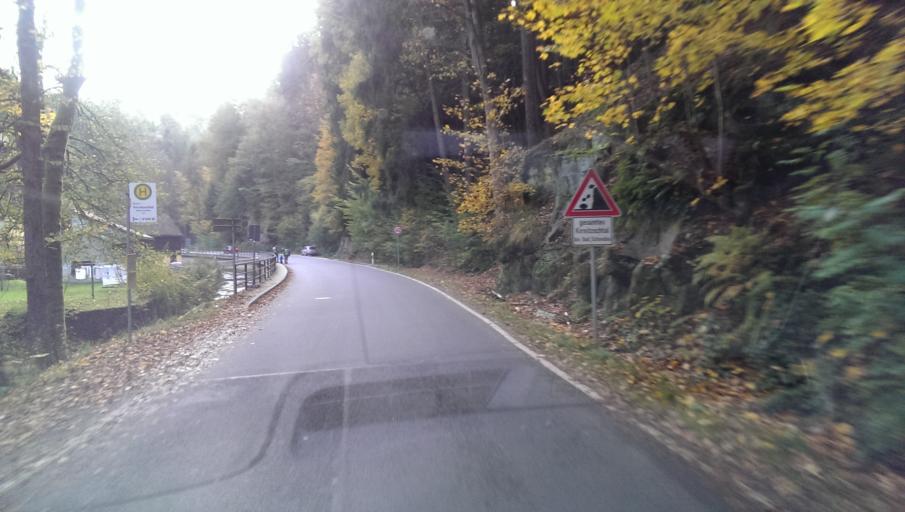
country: DE
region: Saxony
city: Sebnitz
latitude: 50.9254
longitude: 14.2883
